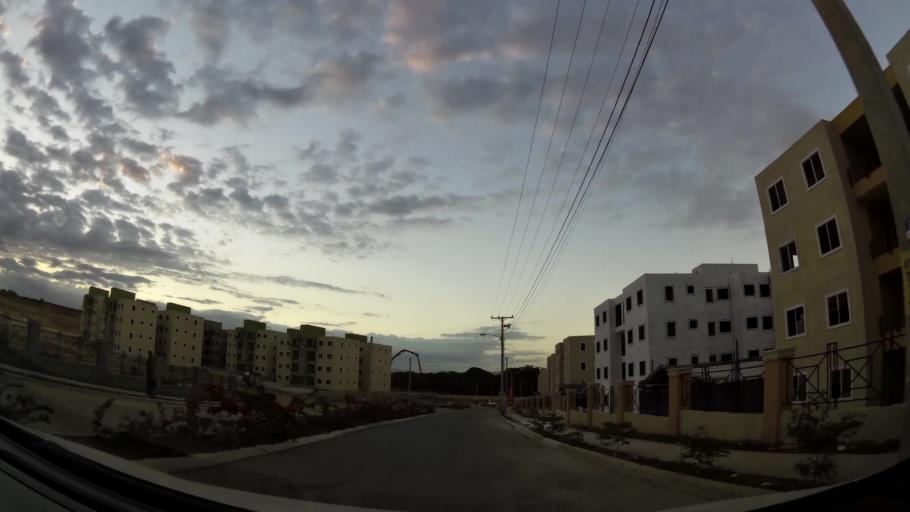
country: DO
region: Nacional
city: La Agustina
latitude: 18.5646
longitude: -69.9455
